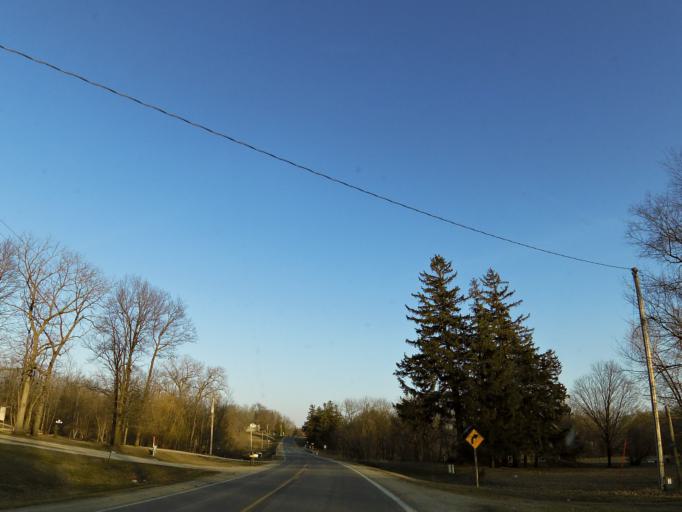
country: US
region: Iowa
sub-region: Mitchell County
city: Saint Ansgar
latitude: 43.3844
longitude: -92.9326
